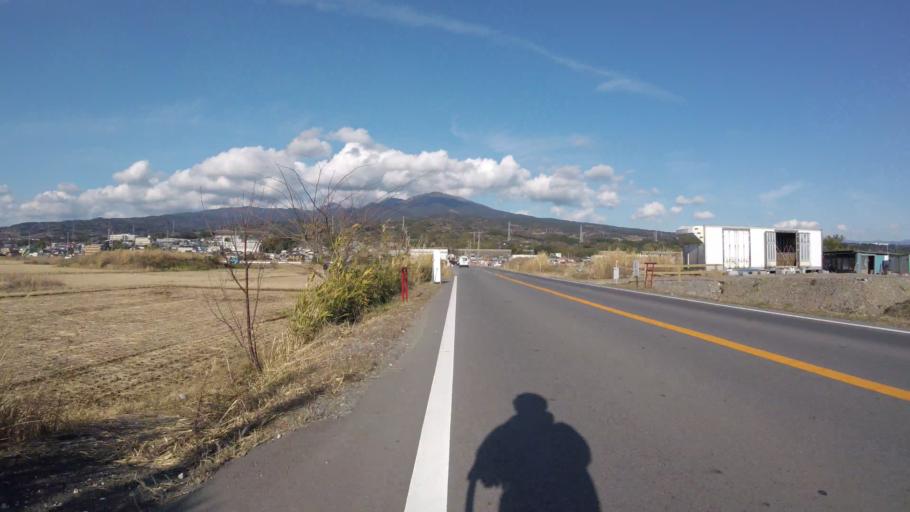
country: JP
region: Shizuoka
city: Numazu
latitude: 35.1415
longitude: 138.7855
